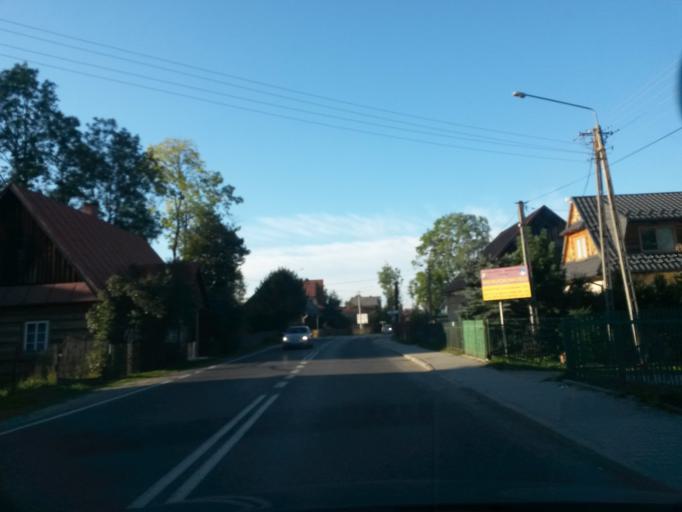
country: PL
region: Lesser Poland Voivodeship
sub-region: Powiat tatrzanski
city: Koscielisko
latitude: 49.3254
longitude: 19.8244
